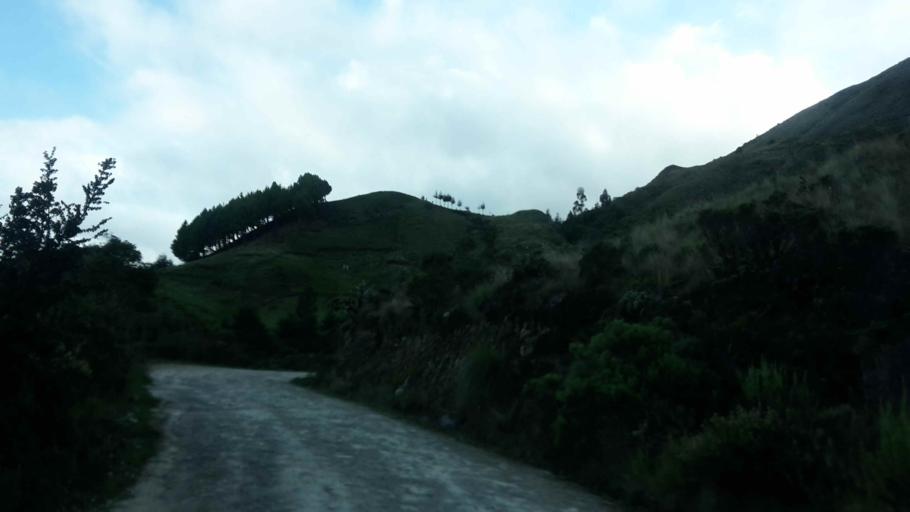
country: BO
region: Cochabamba
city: Colomi
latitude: -17.2402
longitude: -65.9051
